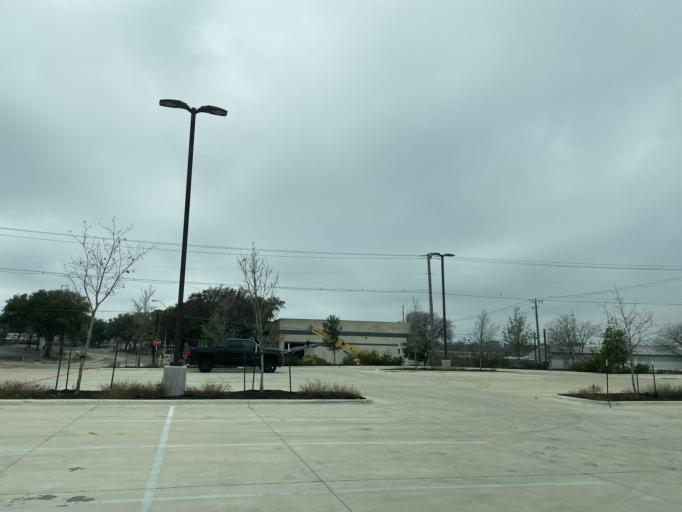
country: US
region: Texas
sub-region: Williamson County
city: Round Rock
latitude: 30.5430
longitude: -97.6885
